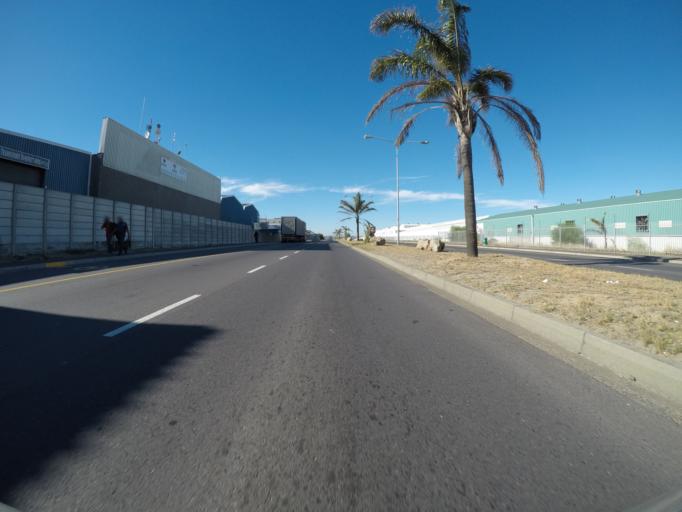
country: ZA
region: Western Cape
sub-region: City of Cape Town
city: Kraaifontein
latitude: -33.9020
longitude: 18.6692
